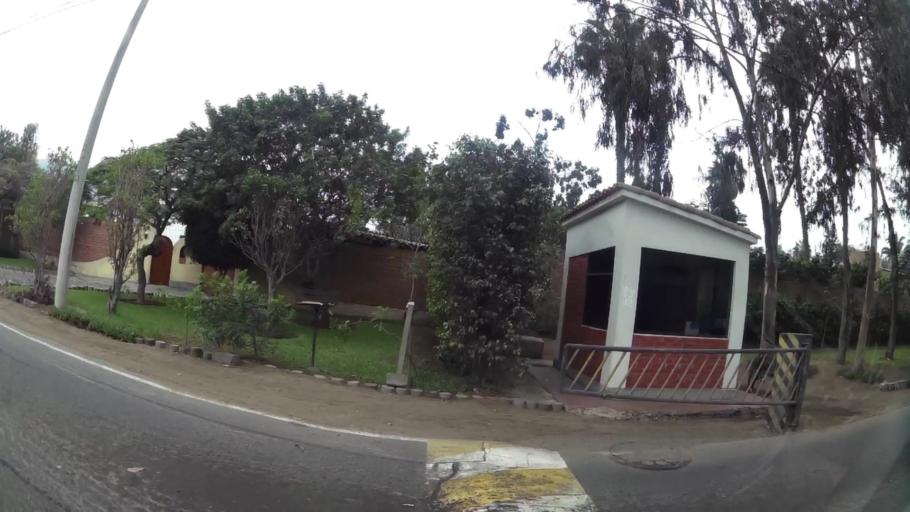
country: PE
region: Lima
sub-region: Lima
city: La Molina
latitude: -12.0788
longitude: -76.9158
